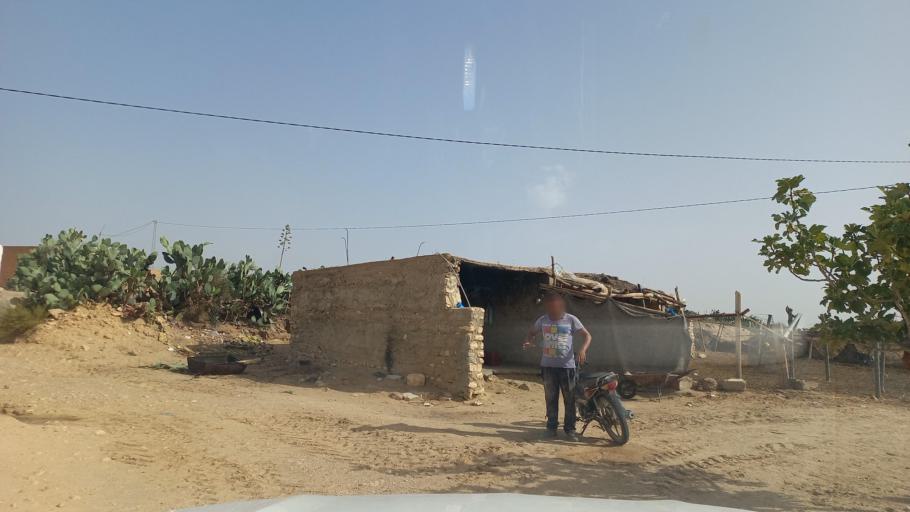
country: TN
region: Al Qasrayn
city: Kasserine
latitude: 35.2976
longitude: 8.9605
